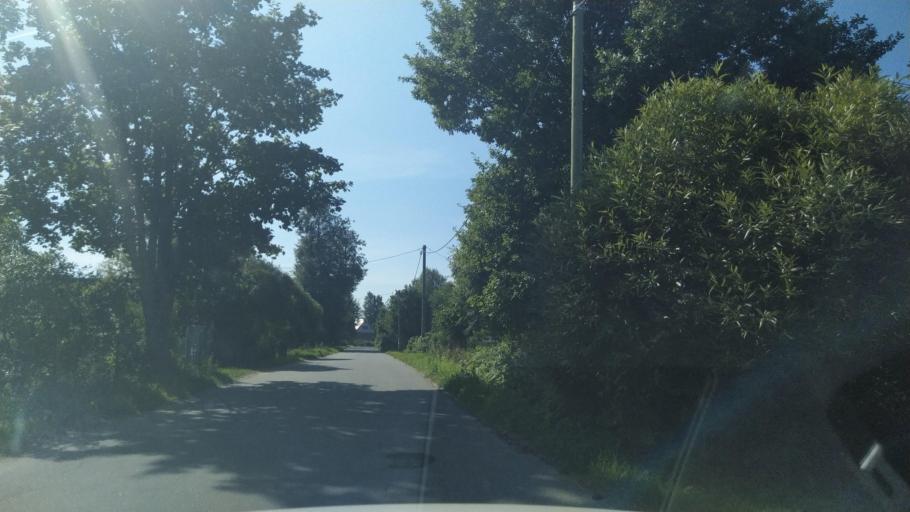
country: RU
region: Leningrad
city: Siverskiy
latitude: 59.2674
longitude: 30.0431
